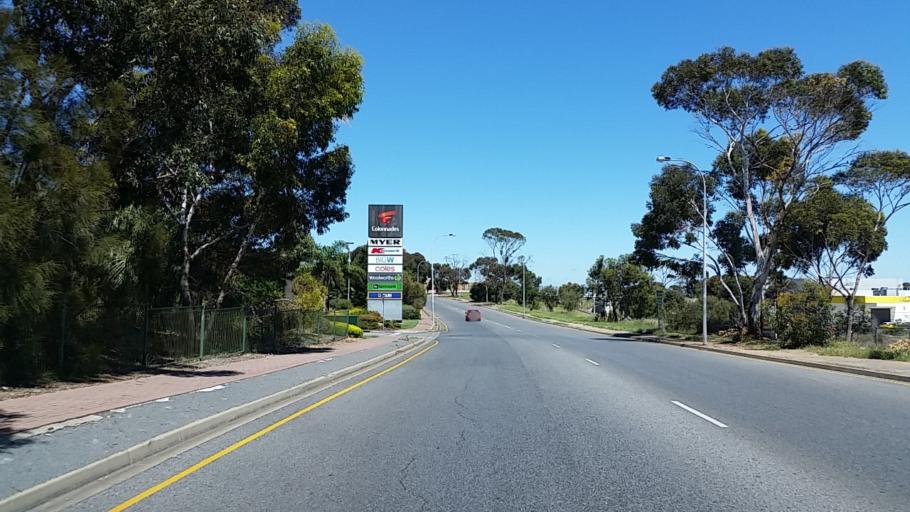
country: AU
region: South Australia
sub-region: Onkaparinga
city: Noarlunga Downs
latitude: -35.1411
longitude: 138.4925
